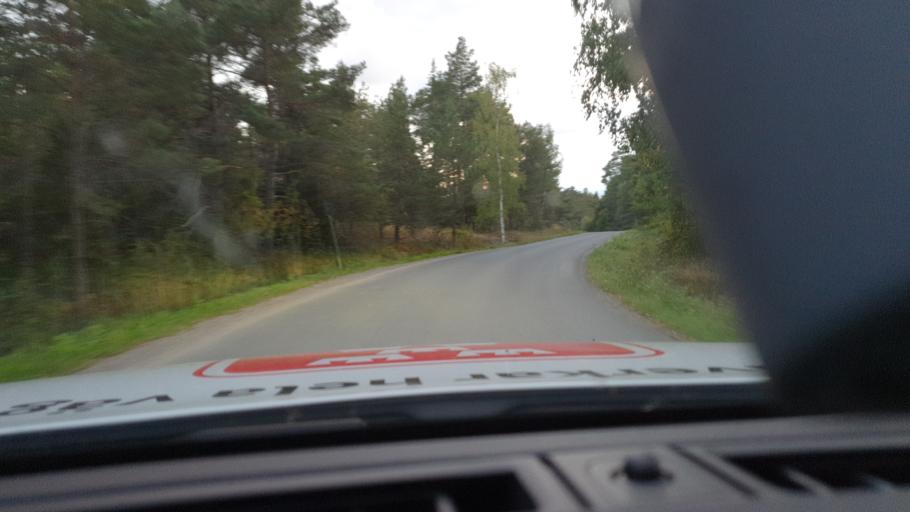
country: SE
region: Stockholm
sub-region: Norrtalje Kommun
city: Norrtalje
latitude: 59.6312
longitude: 18.7108
